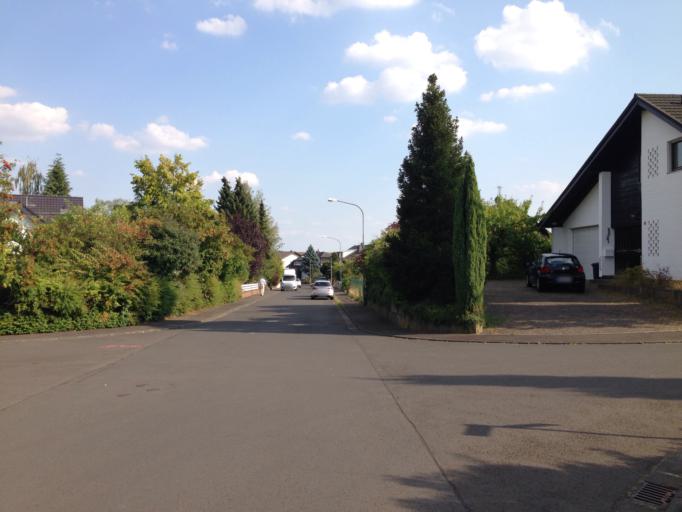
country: DE
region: Hesse
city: Lollar
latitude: 50.6415
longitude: 8.6612
